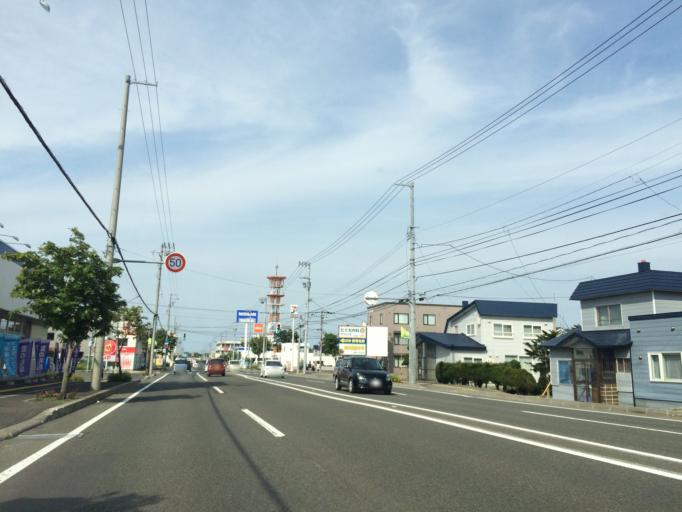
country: JP
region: Hokkaido
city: Ebetsu
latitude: 43.1077
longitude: 141.5443
